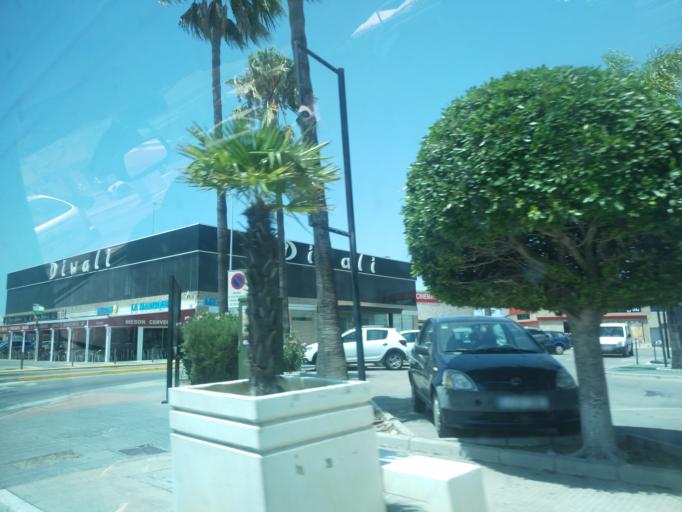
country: ES
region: Andalusia
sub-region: Provincia de Cadiz
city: Chiclana de la Frontera
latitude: 36.4300
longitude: -6.1445
